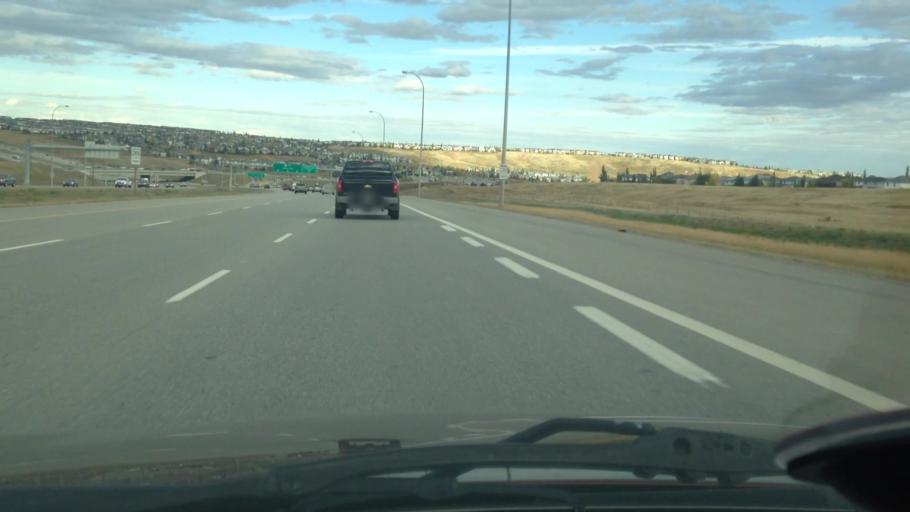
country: CA
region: Alberta
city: Calgary
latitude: 51.1529
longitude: -114.1270
